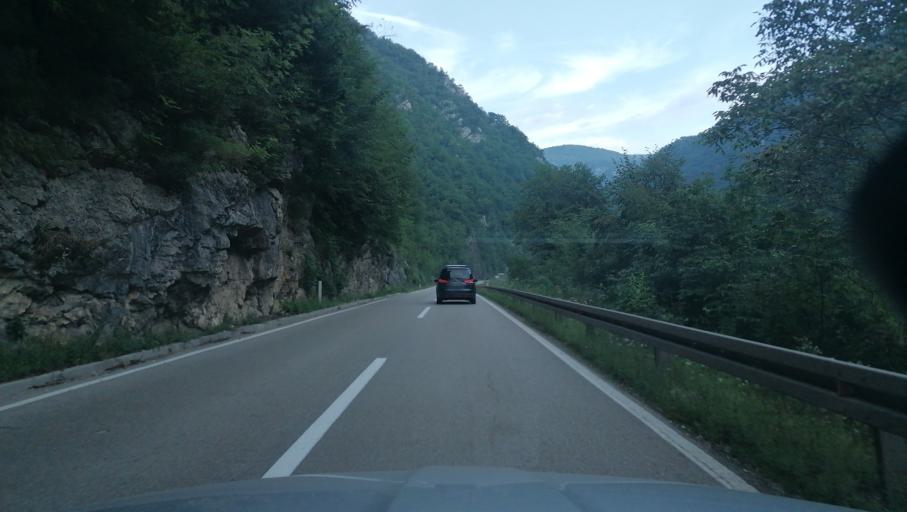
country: BA
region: Federation of Bosnia and Herzegovina
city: Jajce
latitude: 44.4400
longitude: 17.2343
